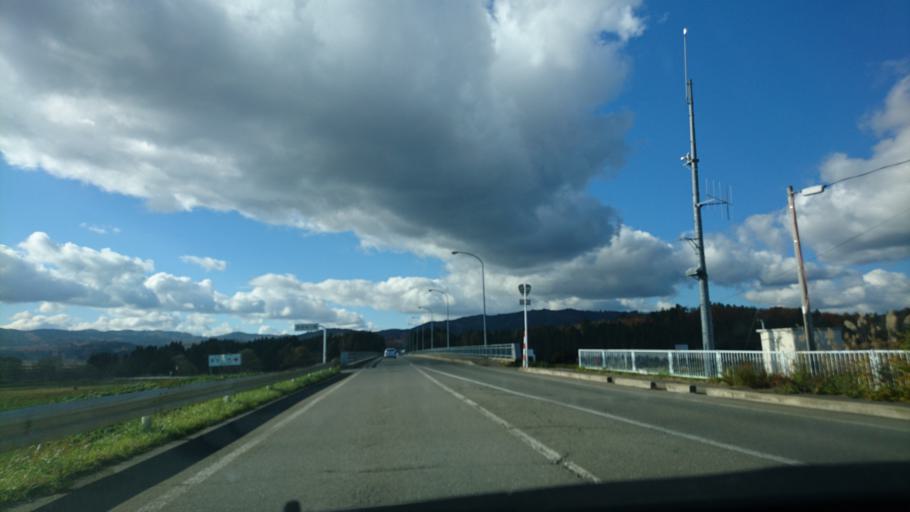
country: JP
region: Akita
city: Yuzawa
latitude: 39.2756
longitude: 140.4046
